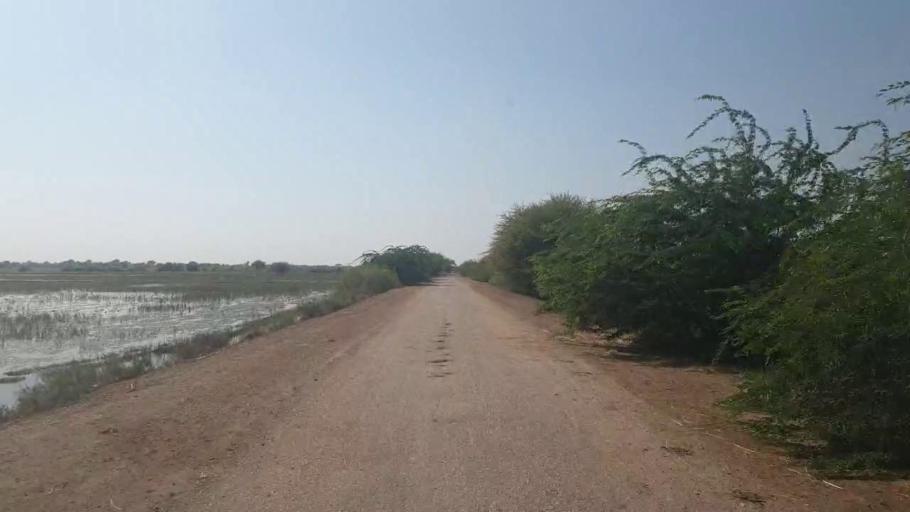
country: PK
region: Sindh
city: Badin
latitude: 24.5549
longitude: 68.8222
